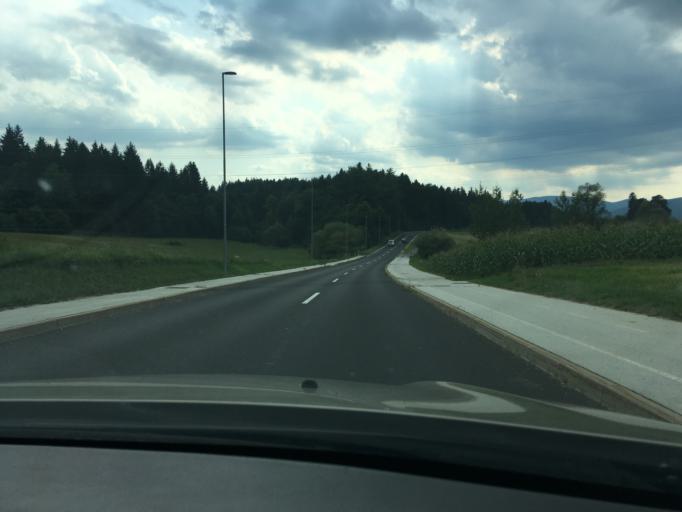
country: SI
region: Novo Mesto
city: Novo Mesto
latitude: 45.7943
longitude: 15.1438
